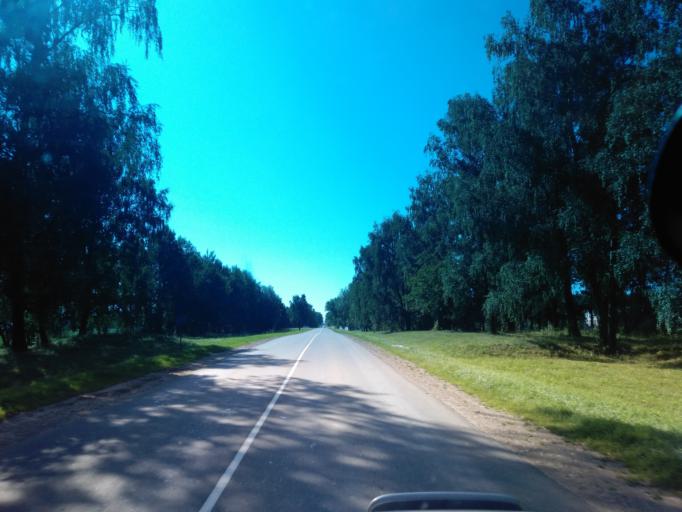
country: BY
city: Fanipol
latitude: 53.7137
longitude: 27.3445
